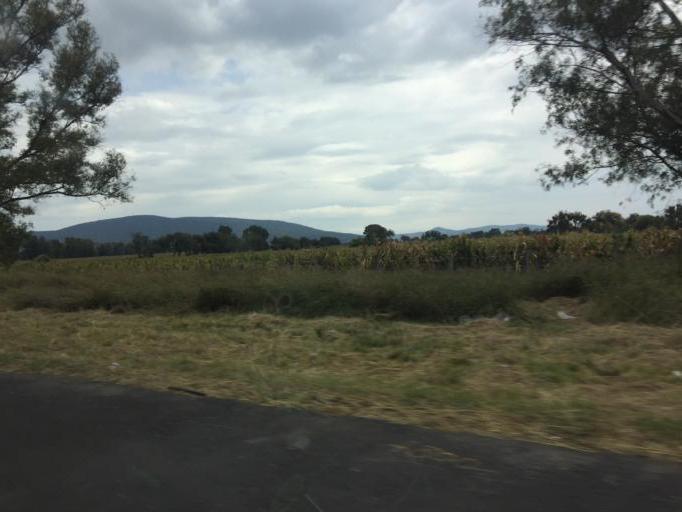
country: MX
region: Jalisco
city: Ocotlan
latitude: 20.3894
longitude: -102.7151
